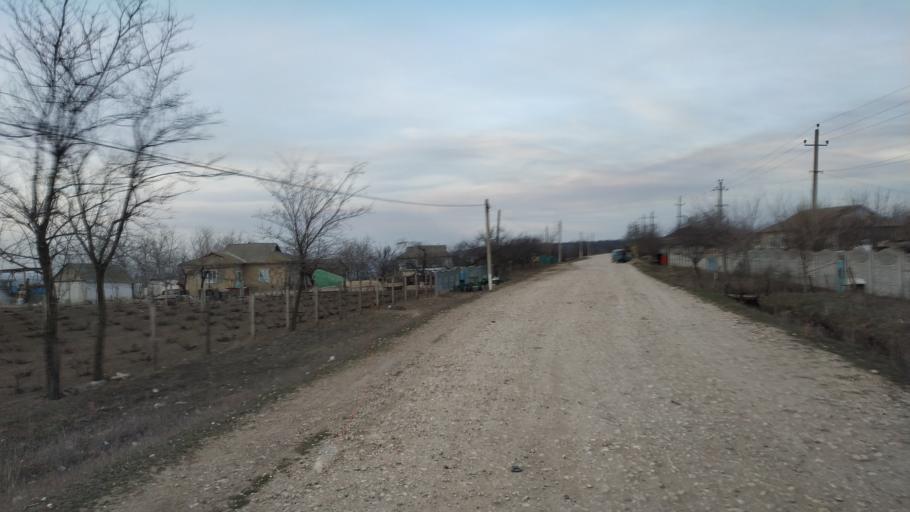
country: MD
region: Hincesti
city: Dancu
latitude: 46.7478
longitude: 28.2091
